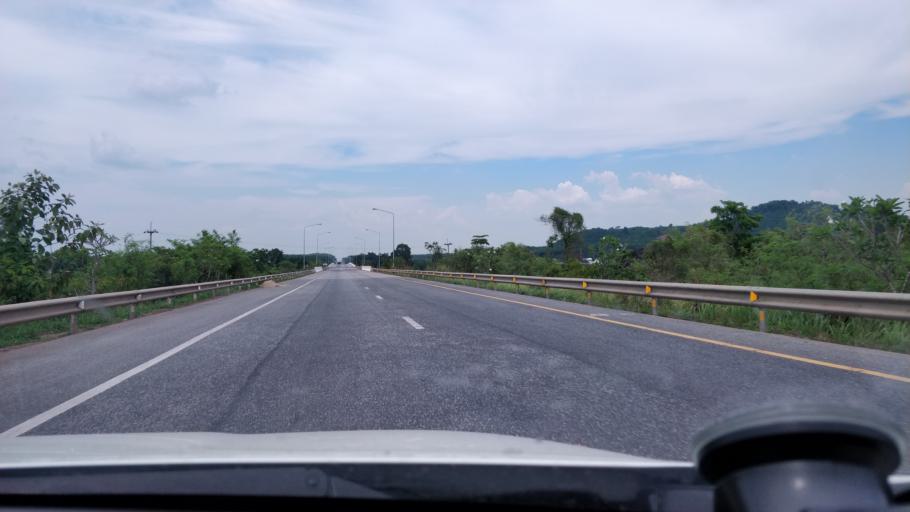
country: TH
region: Surat Thani
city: Khian Sa
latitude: 8.8631
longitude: 99.1929
